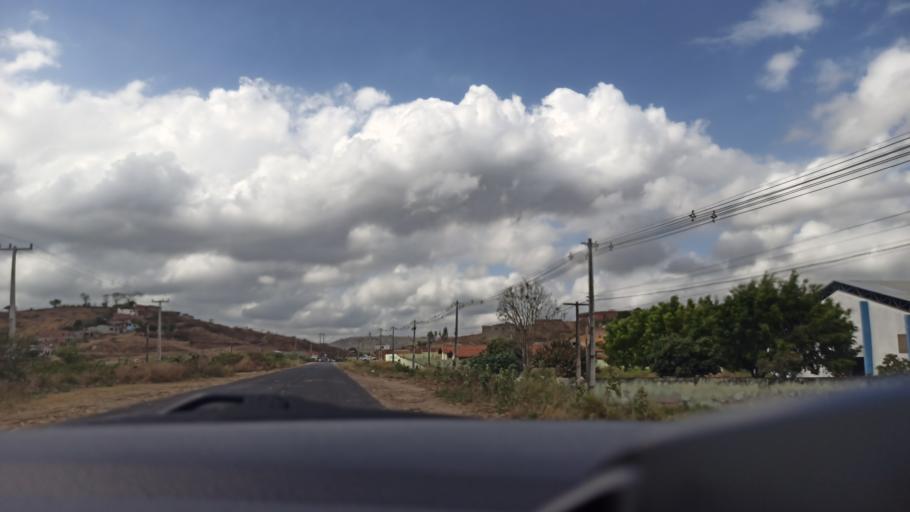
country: BR
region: Pernambuco
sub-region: Timbauba
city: Timbauba
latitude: -7.5010
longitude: -35.2987
